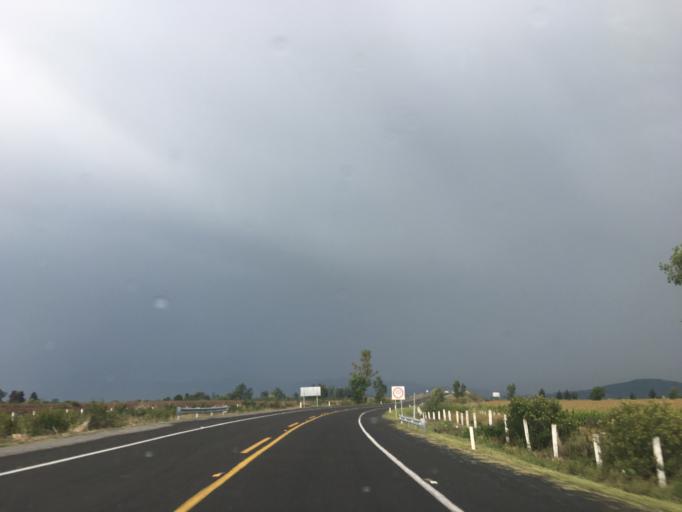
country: MX
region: Michoacan
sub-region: Alvaro Obregon
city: Lazaro Cardenas (La Purisima)
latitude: 19.8762
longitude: -101.0076
